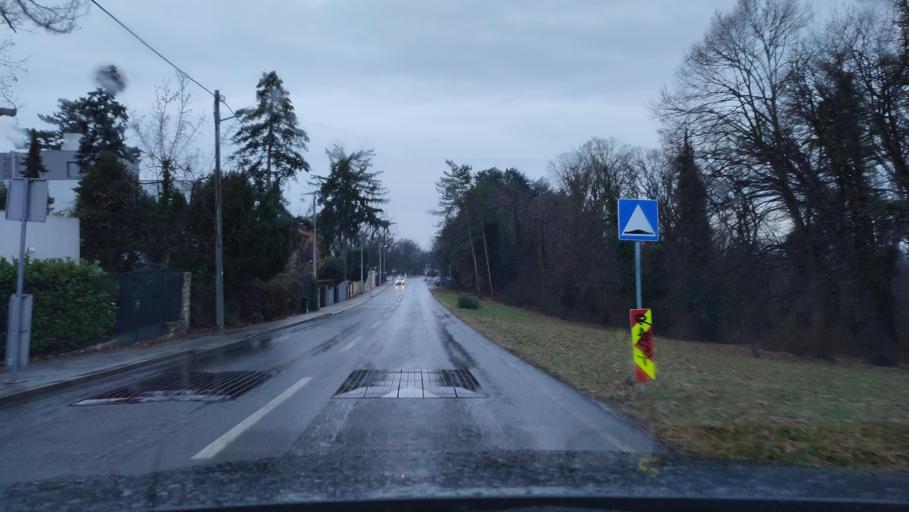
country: HR
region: Grad Zagreb
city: Zagreb
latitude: 45.8377
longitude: 15.9708
